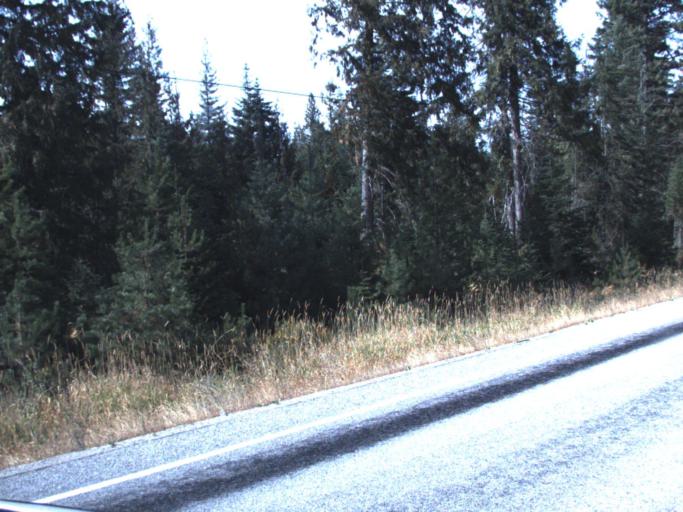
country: US
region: Washington
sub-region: Pend Oreille County
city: Newport
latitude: 48.2618
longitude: -117.2845
